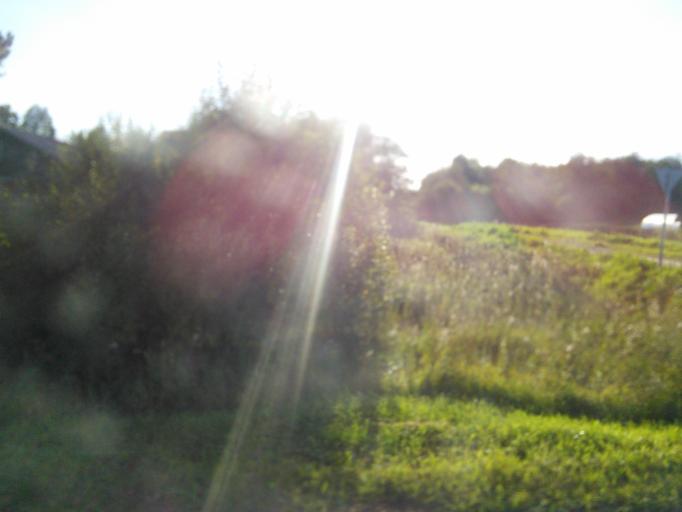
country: RU
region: Jaroslavl
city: Poshekhon'ye
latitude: 58.4527
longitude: 39.0350
